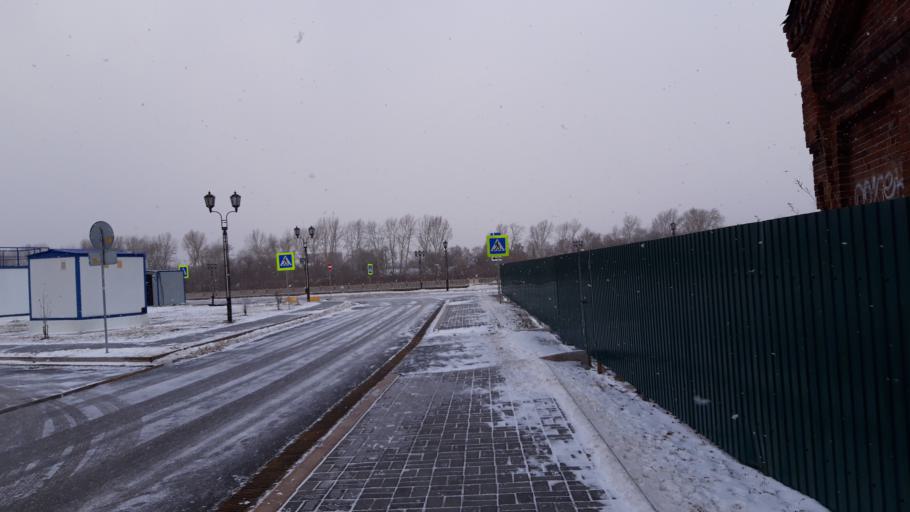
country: RU
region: Tjumen
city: Tyumen
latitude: 57.1616
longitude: 65.5500
